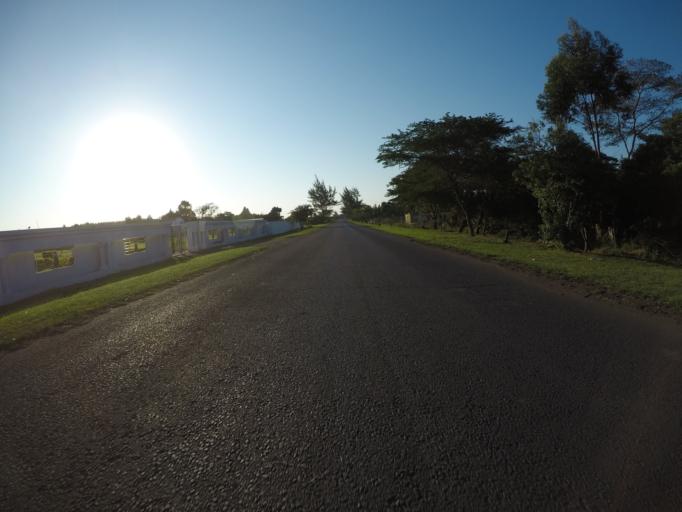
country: ZA
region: KwaZulu-Natal
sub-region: uThungulu District Municipality
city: KwaMbonambi
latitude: -28.6885
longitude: 32.2071
